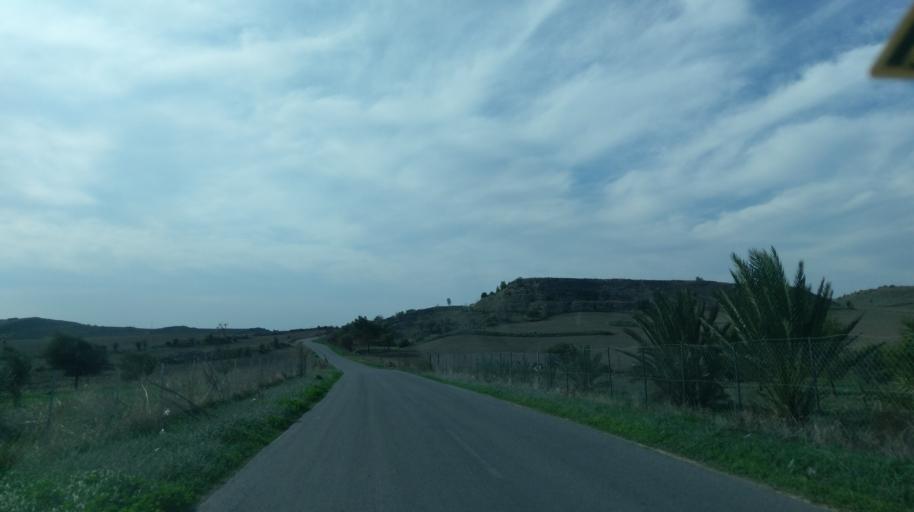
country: CY
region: Keryneia
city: Lapithos
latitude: 35.2809
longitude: 33.2034
